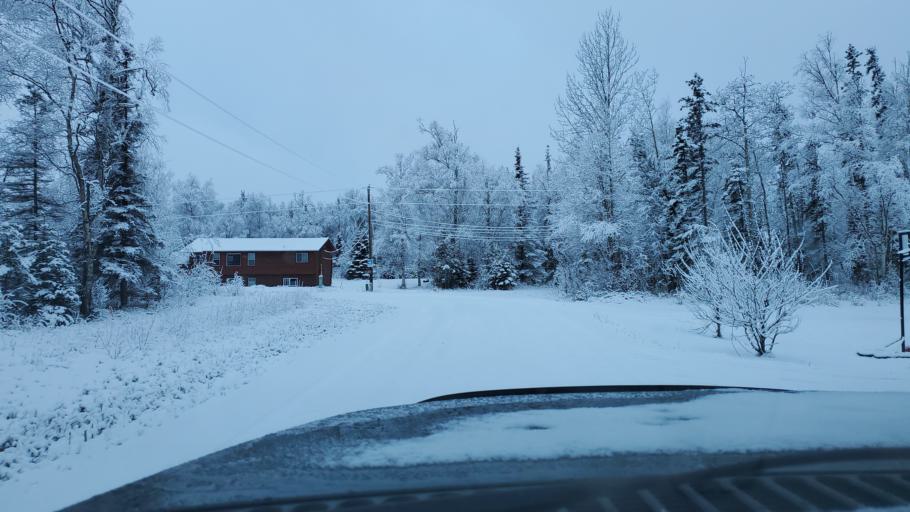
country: US
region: Alaska
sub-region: Matanuska-Susitna Borough
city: Wasilla
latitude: 61.5917
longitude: -149.4125
